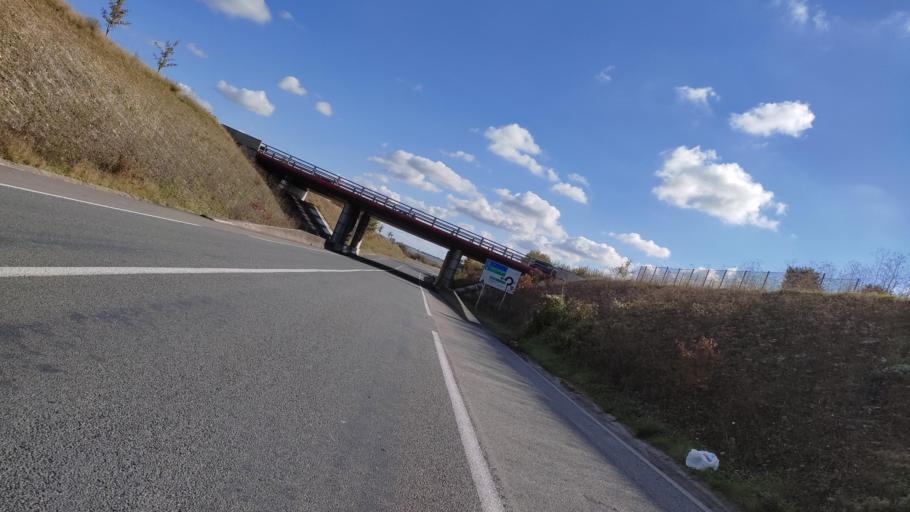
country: FR
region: Nord-Pas-de-Calais
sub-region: Departement du Pas-de-Calais
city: Feuchy
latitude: 50.3110
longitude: 2.8270
